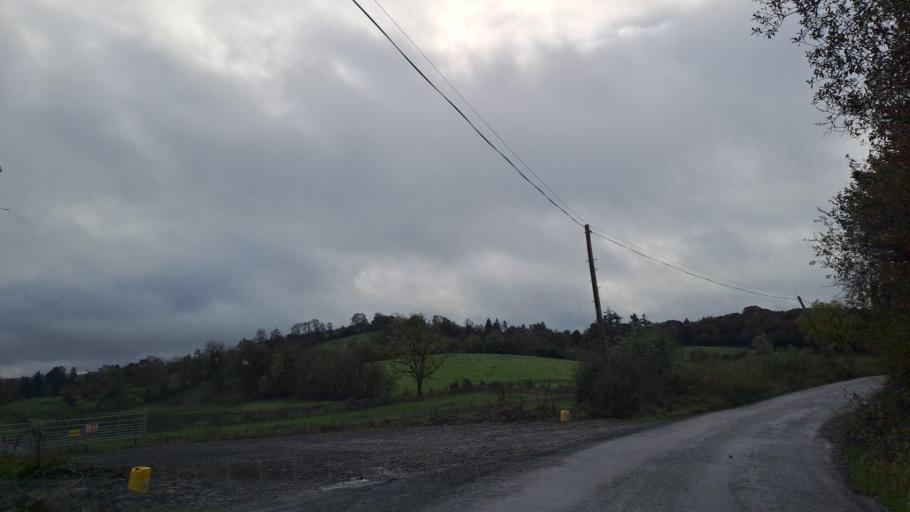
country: IE
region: Ulster
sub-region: An Cabhan
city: Bailieborough
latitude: 53.9447
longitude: -6.9794
